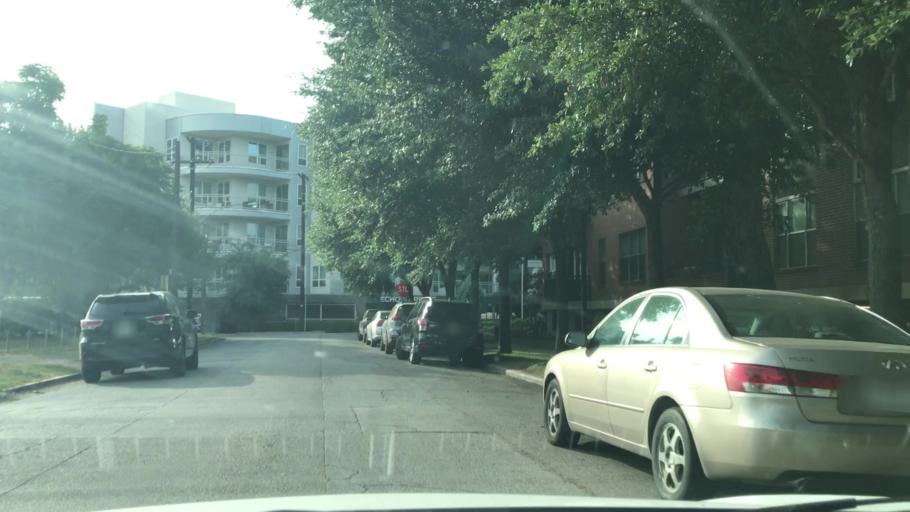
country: US
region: Texas
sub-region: Dallas County
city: Highland Park
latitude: 32.8139
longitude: -96.8166
